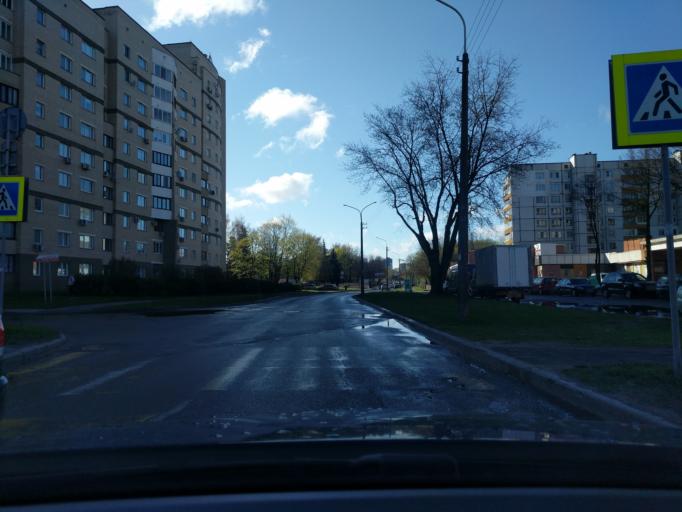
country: BY
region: Minsk
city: Novoye Medvezhino
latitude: 53.9012
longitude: 27.5052
